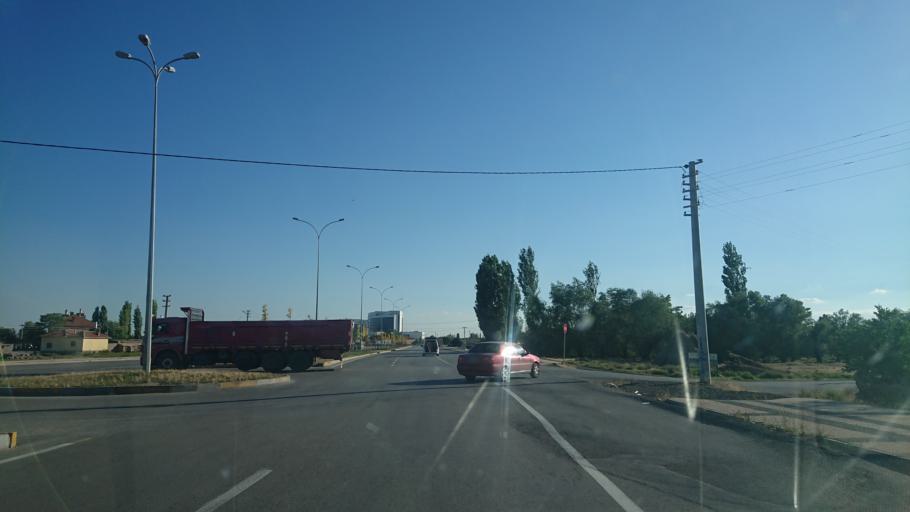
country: TR
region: Aksaray
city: Aksaray
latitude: 38.3801
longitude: 33.9898
